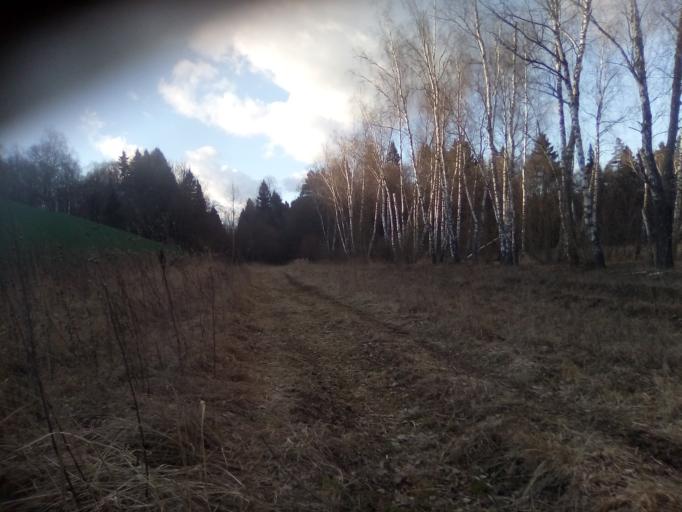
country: RU
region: Moskovskaya
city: Filimonki
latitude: 55.5799
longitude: 37.3355
